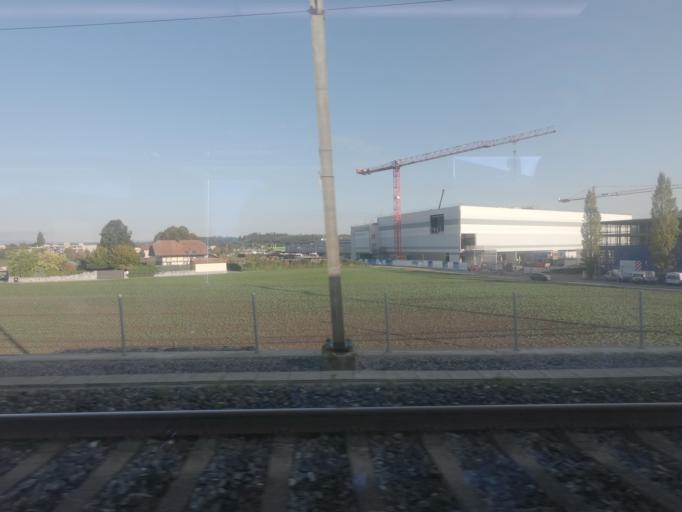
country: CH
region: Bern
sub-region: Bern-Mittelland District
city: Urtenen
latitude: 47.0132
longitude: 7.4907
